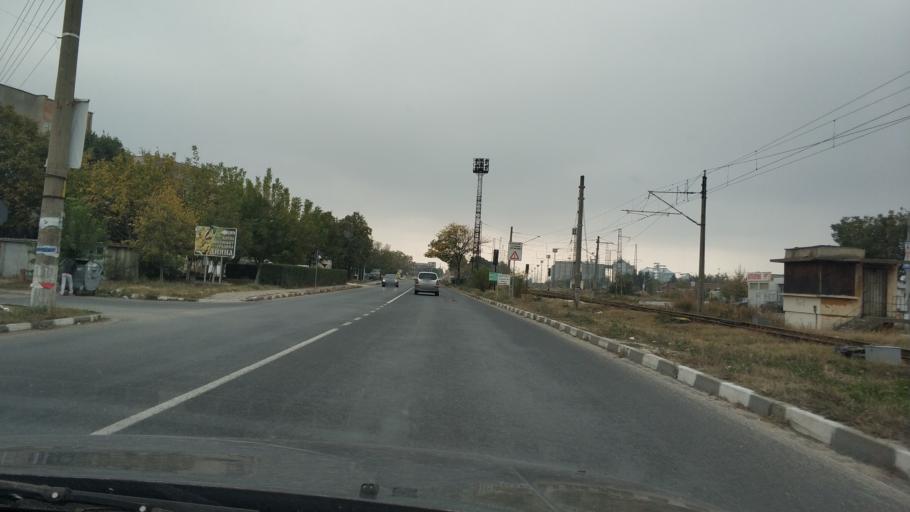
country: BG
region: Plovdiv
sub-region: Obshtina Plovdiv
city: Plovdiv
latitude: 42.2339
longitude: 24.7236
